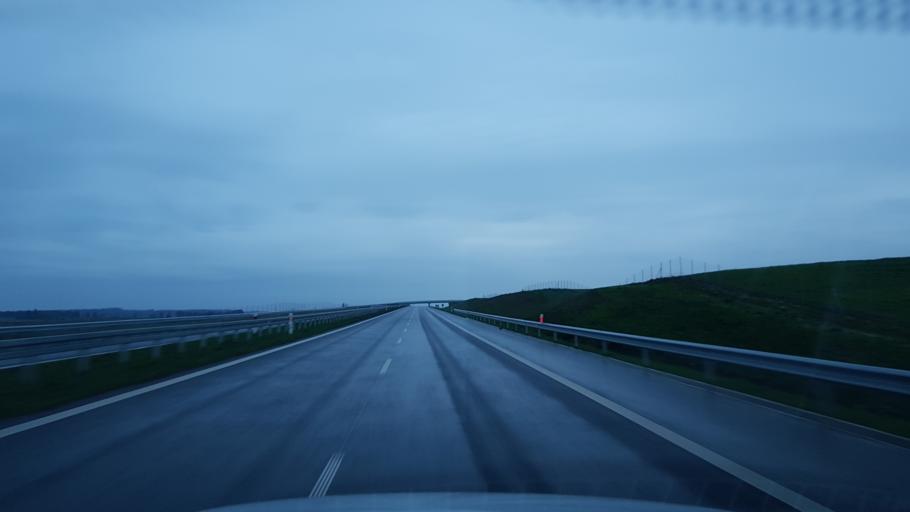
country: PL
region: West Pomeranian Voivodeship
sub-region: Powiat gryficki
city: Brojce
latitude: 53.9728
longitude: 15.4262
